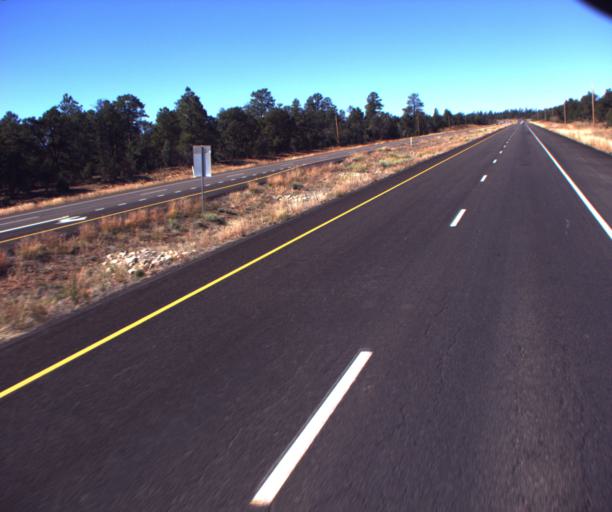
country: US
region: Arizona
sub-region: Apache County
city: Saint Michaels
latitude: 35.6605
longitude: -109.1580
